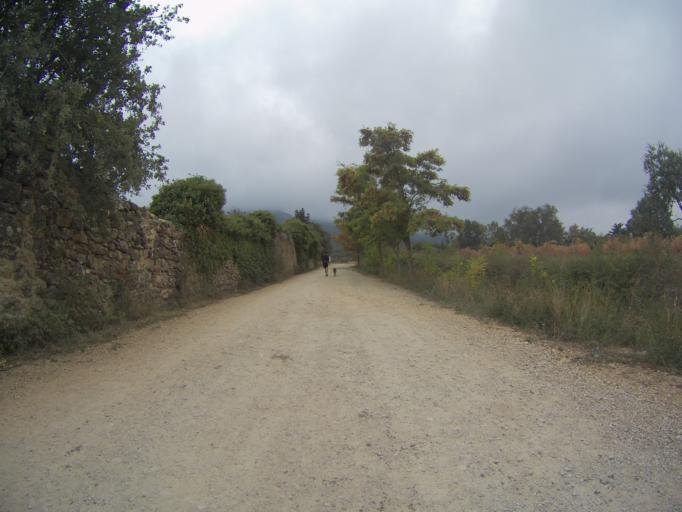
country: ES
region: Navarre
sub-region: Provincia de Navarra
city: Ayegui
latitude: 42.6474
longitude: -2.0477
